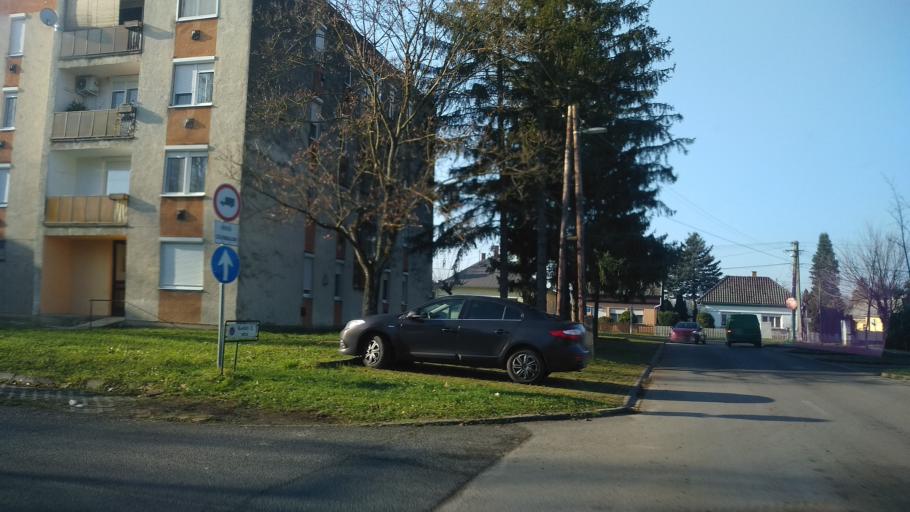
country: HU
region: Somogy
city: Barcs
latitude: 45.9590
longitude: 17.4502
